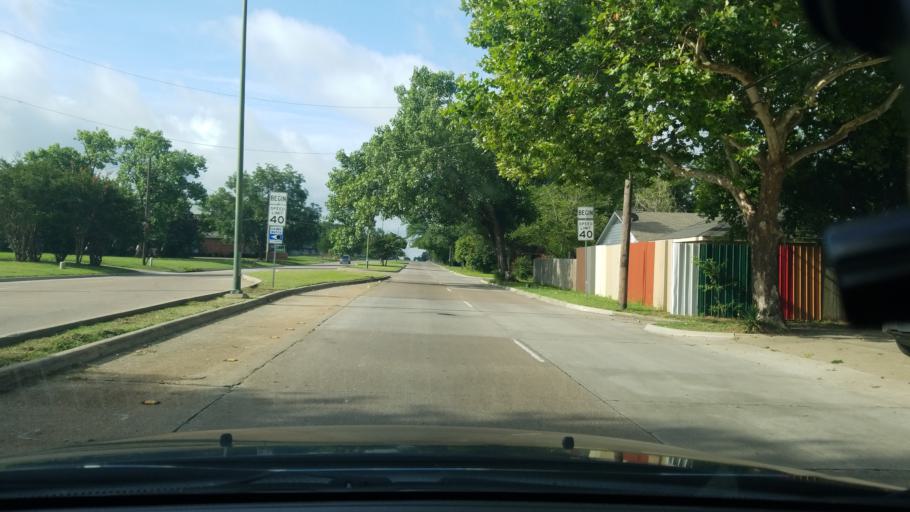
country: US
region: Texas
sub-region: Dallas County
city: Mesquite
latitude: 32.8212
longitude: -96.6655
